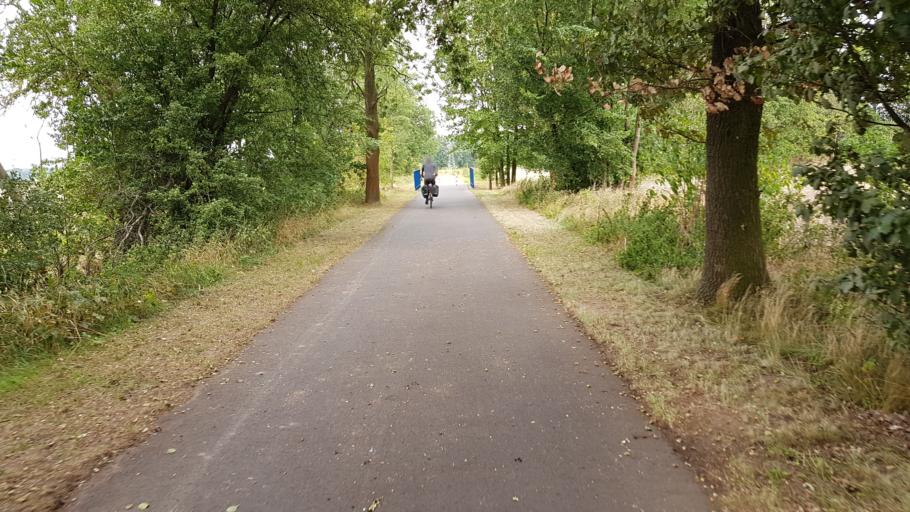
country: PL
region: West Pomeranian Voivodeship
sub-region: Powiat pyrzycki
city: Pyrzyce
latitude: 53.1421
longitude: 14.9618
